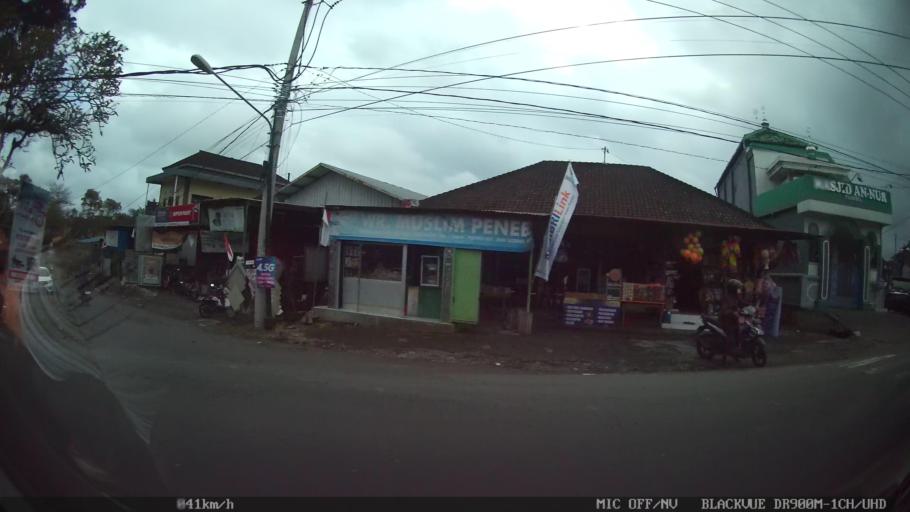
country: ID
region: Bali
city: Penebel
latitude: -8.4256
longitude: 115.1443
